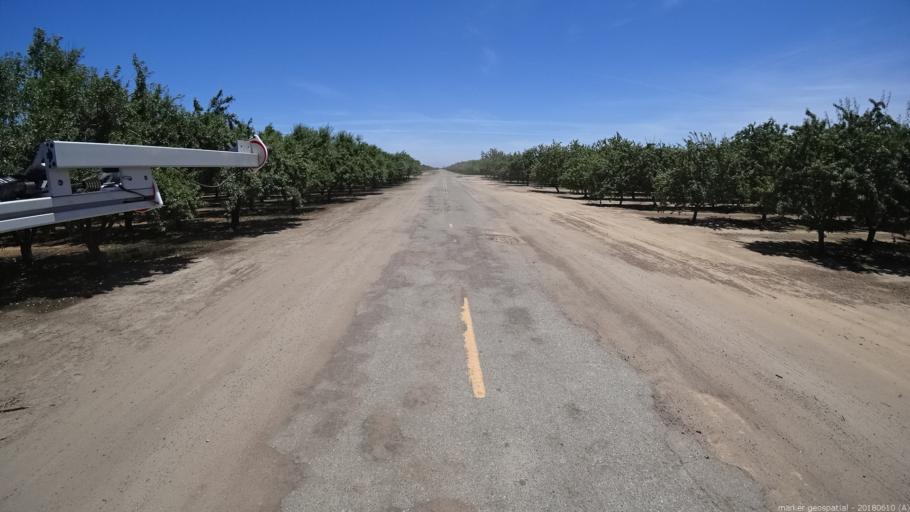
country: US
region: California
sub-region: Madera County
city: Chowchilla
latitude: 37.0473
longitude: -120.2756
